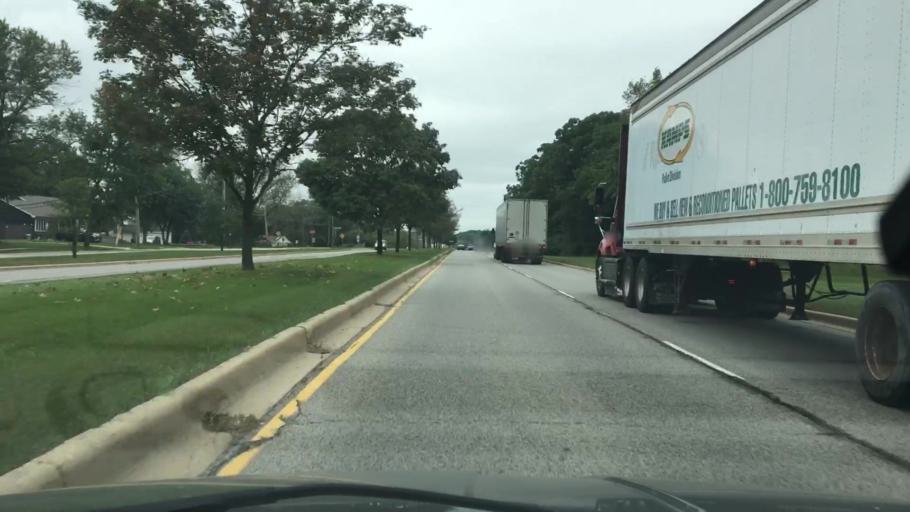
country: US
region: Illinois
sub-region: DuPage County
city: Woodridge
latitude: 41.7501
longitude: -88.0551
